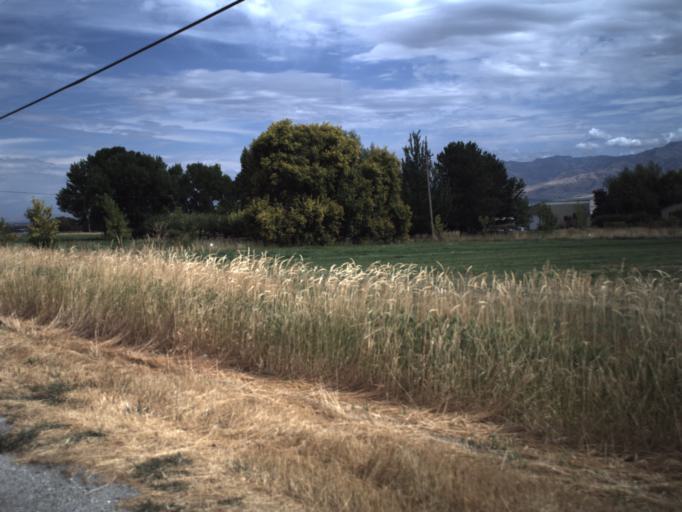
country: US
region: Utah
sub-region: Cache County
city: Mendon
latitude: 41.7205
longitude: -111.9790
